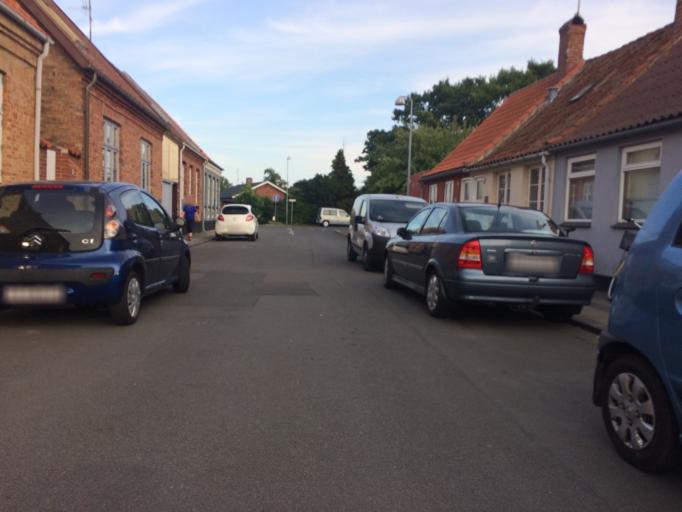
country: DK
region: Capital Region
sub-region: Bornholm Kommune
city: Ronne
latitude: 55.0971
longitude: 14.7047
